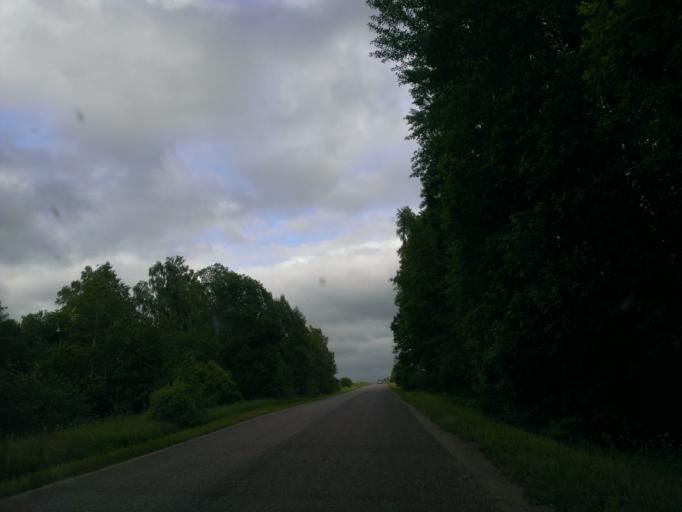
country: LV
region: Aizpute
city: Aizpute
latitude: 56.7074
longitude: 21.7698
